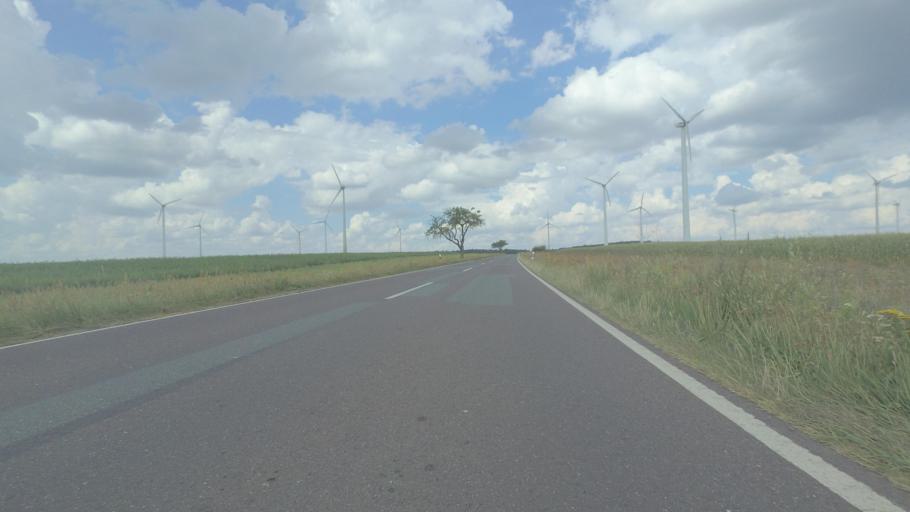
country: DE
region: Brandenburg
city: Wittstock
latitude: 53.2136
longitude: 12.4392
